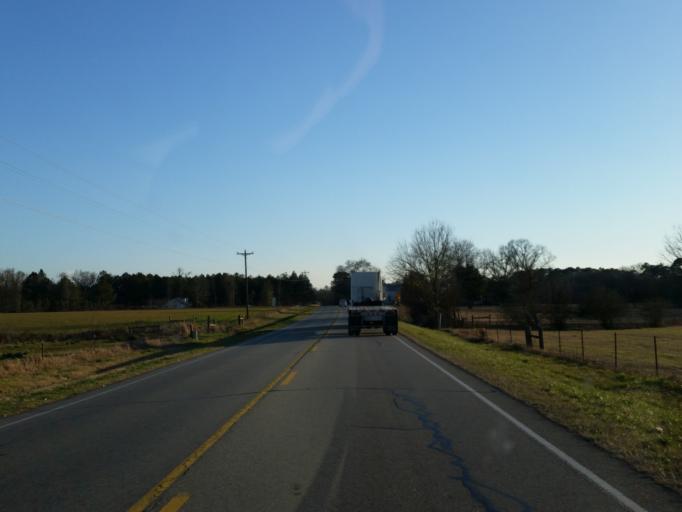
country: US
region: Georgia
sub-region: Dooly County
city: Vienna
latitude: 32.1264
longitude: -83.7975
